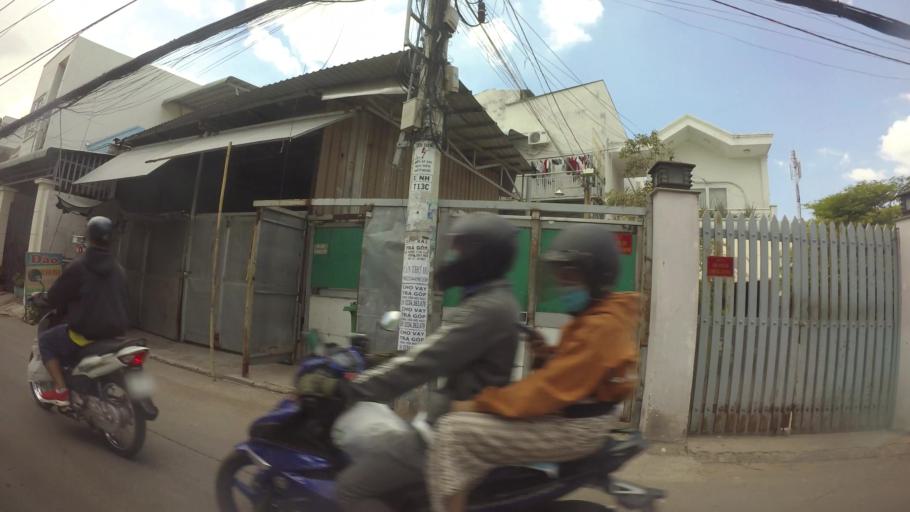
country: VN
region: Ho Chi Minh City
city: Quan Chin
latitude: 10.8223
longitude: 106.7606
